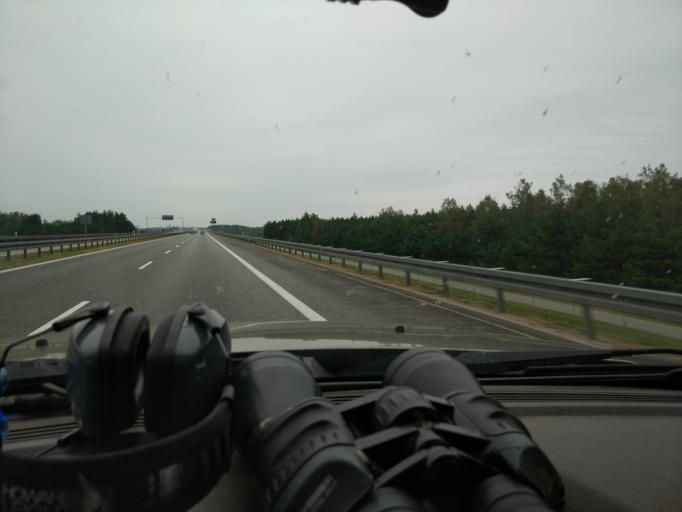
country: PL
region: Masovian Voivodeship
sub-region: Powiat wyszkowski
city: Wyszkow
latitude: 52.5927
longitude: 21.4983
